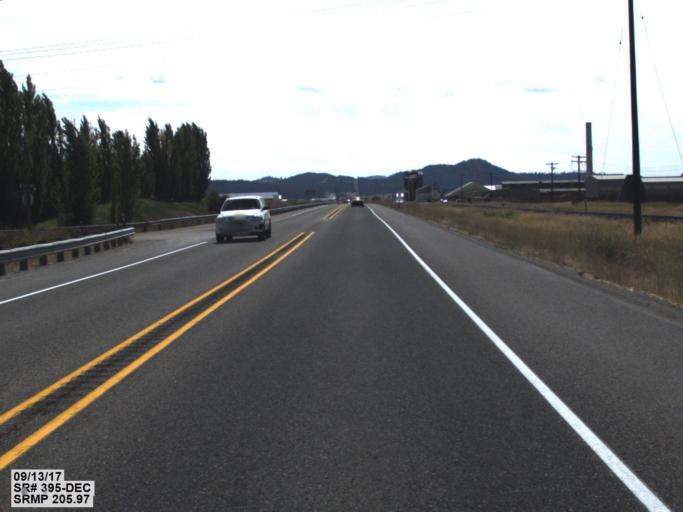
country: US
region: Washington
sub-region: Stevens County
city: Chewelah
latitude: 48.2595
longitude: -117.7154
